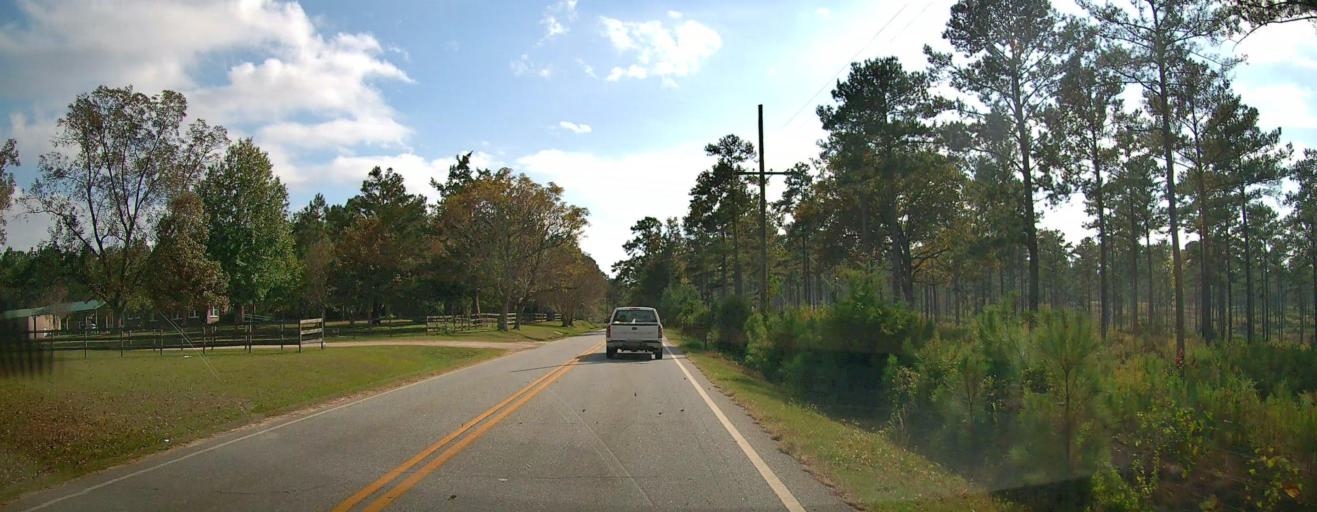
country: US
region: Georgia
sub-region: Thomas County
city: Thomasville
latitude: 30.8997
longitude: -84.0063
